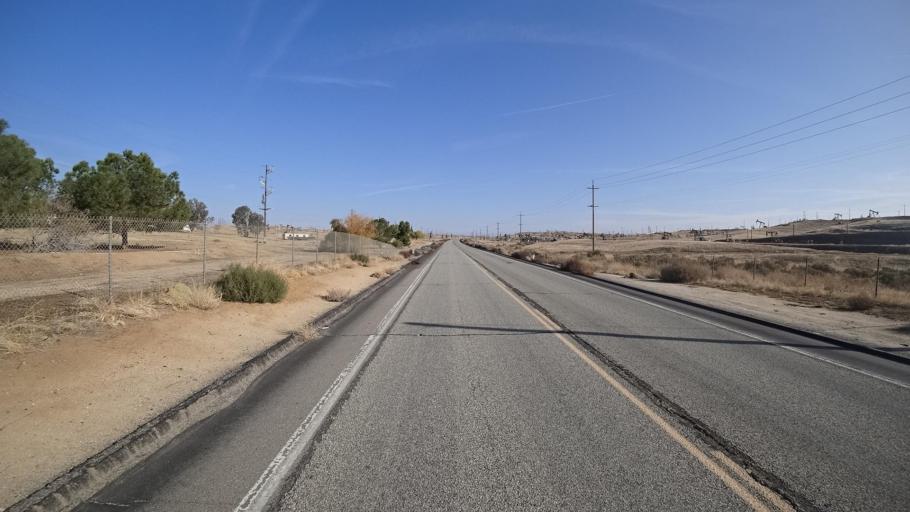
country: US
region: California
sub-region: Kern County
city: Oildale
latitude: 35.4758
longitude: -119.0199
